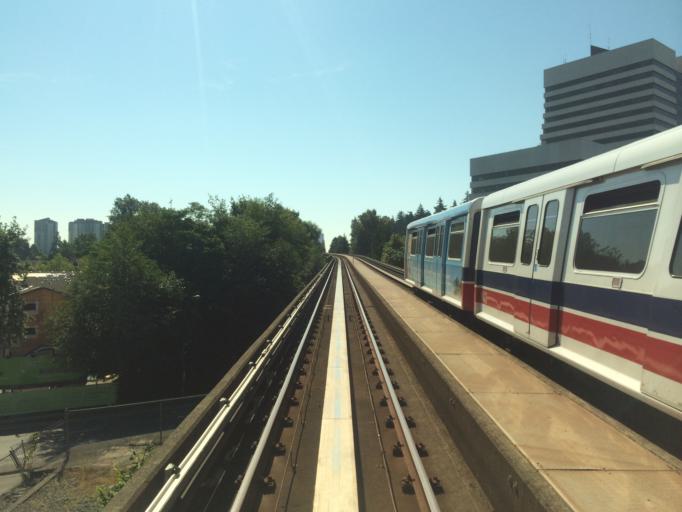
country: CA
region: British Columbia
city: Burnaby
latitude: 49.2347
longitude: -123.0238
